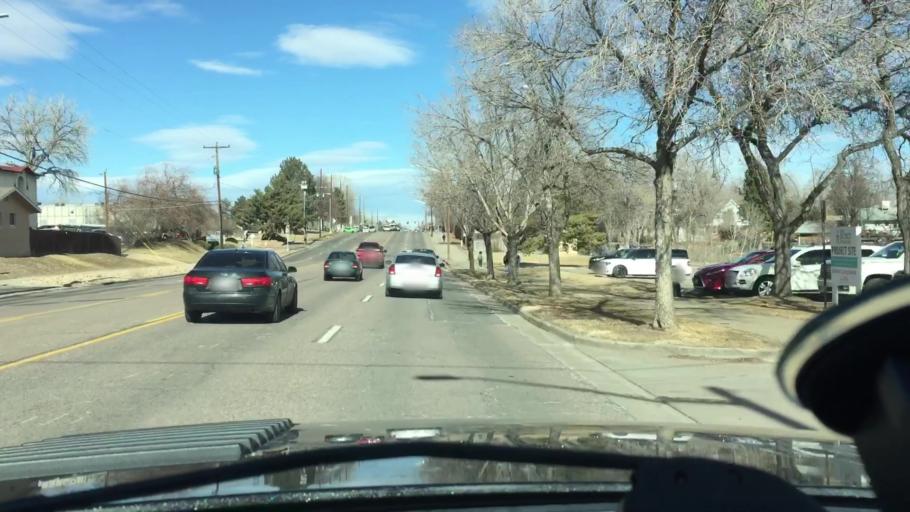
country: US
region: Colorado
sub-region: Adams County
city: Northglenn
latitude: 39.8819
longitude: -104.9966
